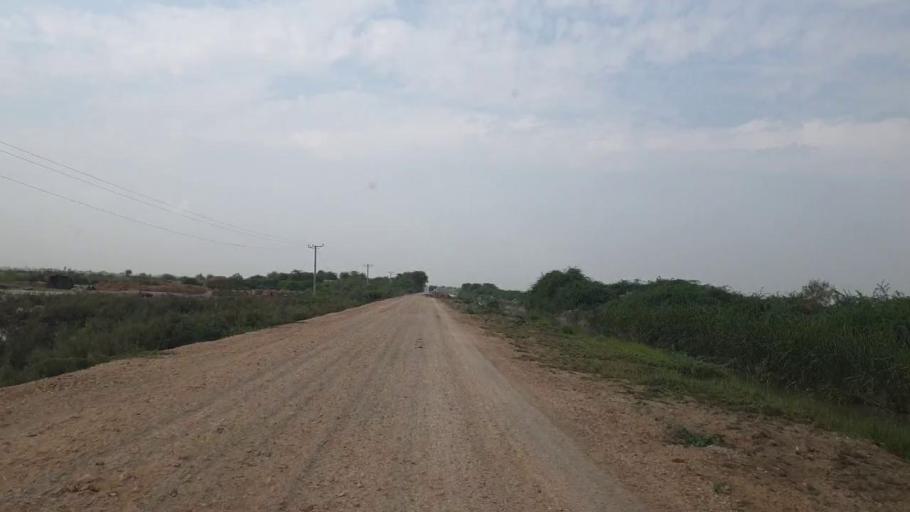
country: PK
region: Sindh
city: Kario
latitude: 24.6204
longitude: 68.5824
